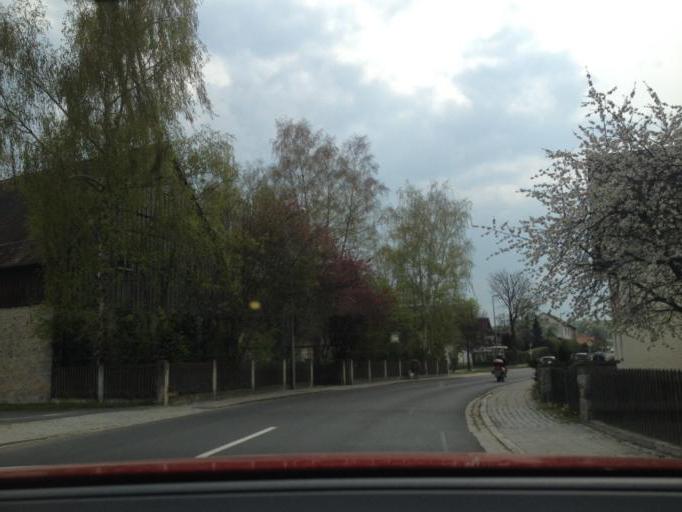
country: DE
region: Bavaria
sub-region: Upper Franconia
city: Goldkronach
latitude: 49.9952
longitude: 11.6611
